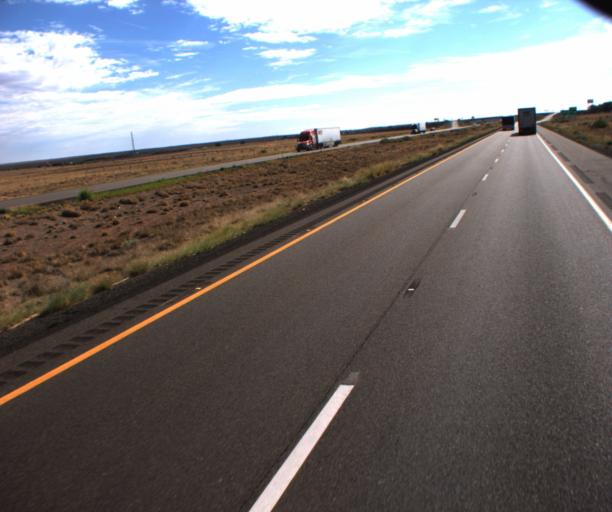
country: US
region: Arizona
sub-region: Navajo County
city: Holbrook
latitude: 34.9785
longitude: -110.0660
